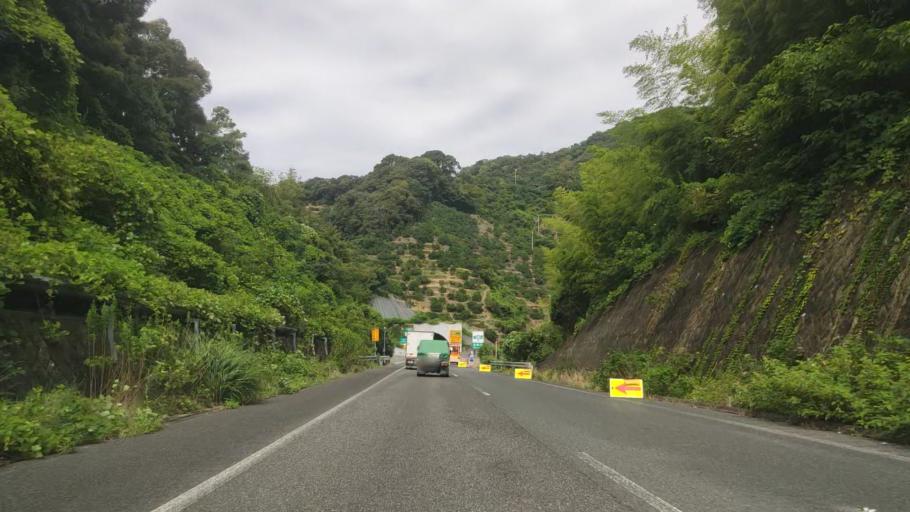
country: JP
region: Wakayama
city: Kainan
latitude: 34.1136
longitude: 135.2000
